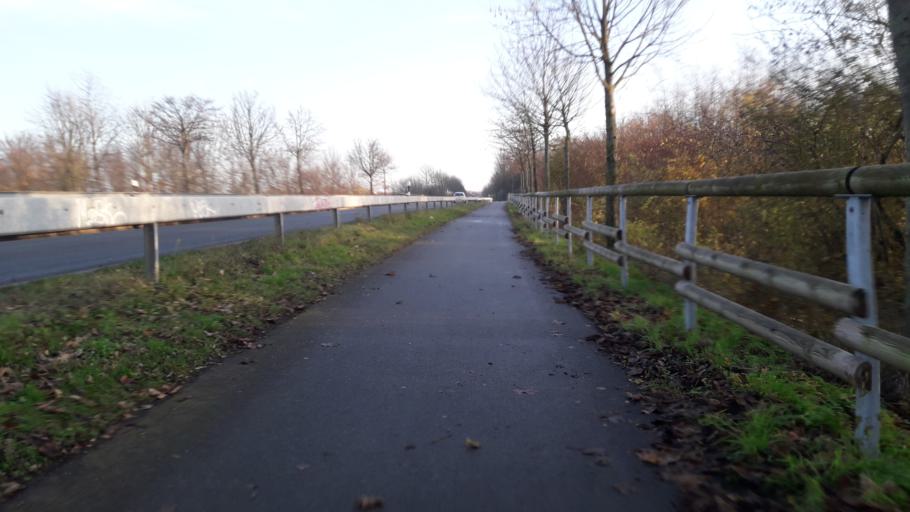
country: DE
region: North Rhine-Westphalia
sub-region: Regierungsbezirk Detmold
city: Paderborn
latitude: 51.7263
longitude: 8.8014
